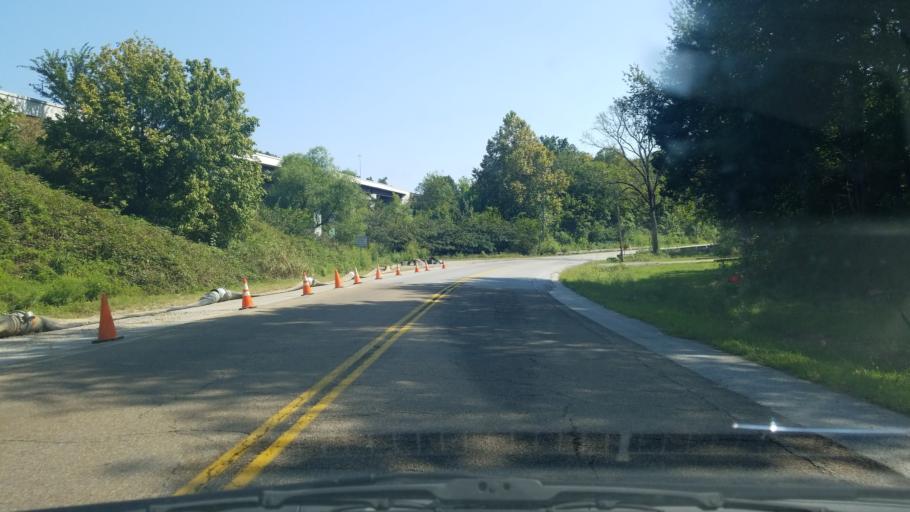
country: US
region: Tennessee
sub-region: Hamilton County
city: Harrison
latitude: 35.0693
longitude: -85.1195
